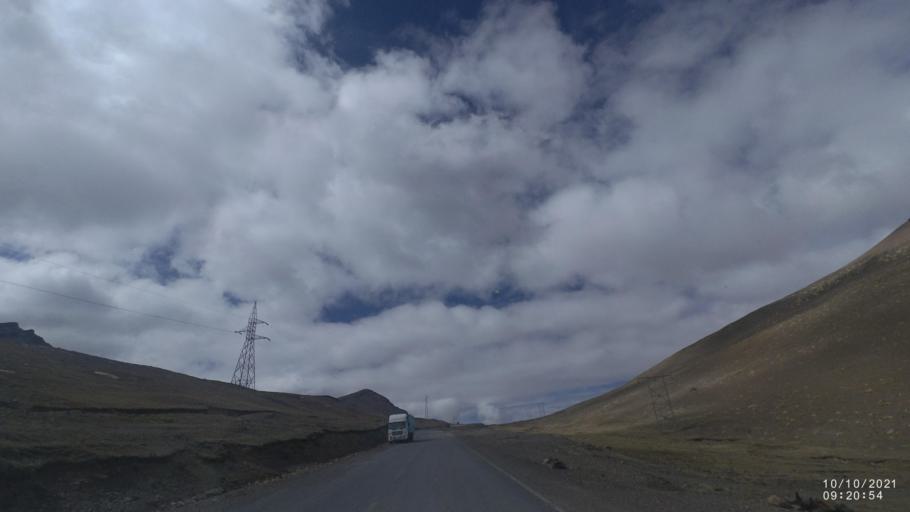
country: BO
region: La Paz
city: Quime
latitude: -17.0632
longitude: -67.2983
